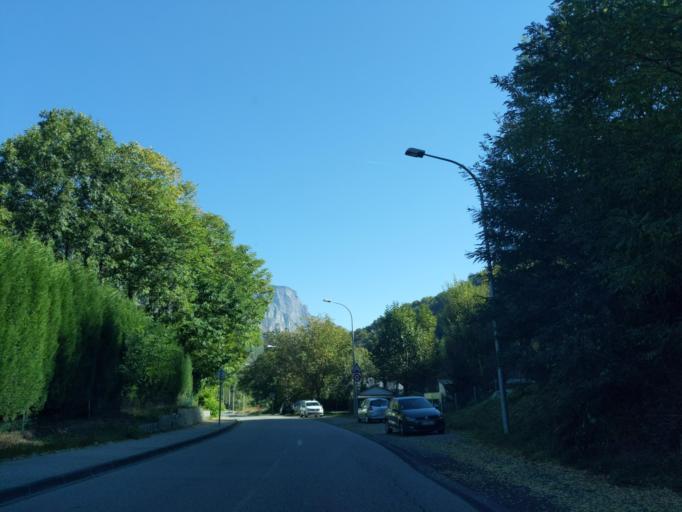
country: FR
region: Rhone-Alpes
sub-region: Departement de la Savoie
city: Villargondran
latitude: 45.2647
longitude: 6.3688
